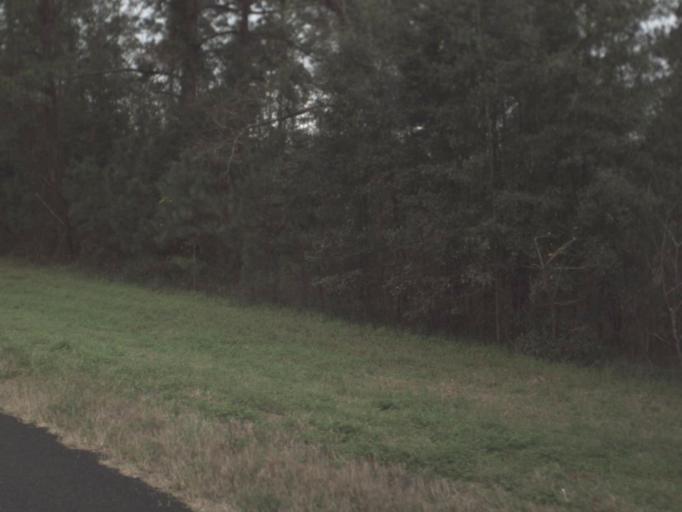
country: US
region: Florida
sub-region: Jefferson County
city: Monticello
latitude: 30.4112
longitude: -83.9278
